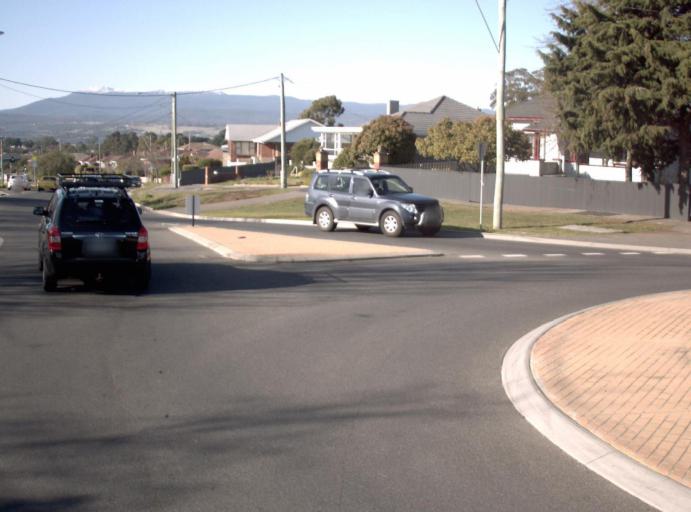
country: AU
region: Tasmania
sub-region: Launceston
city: Summerhill
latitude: -41.4738
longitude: 147.1280
